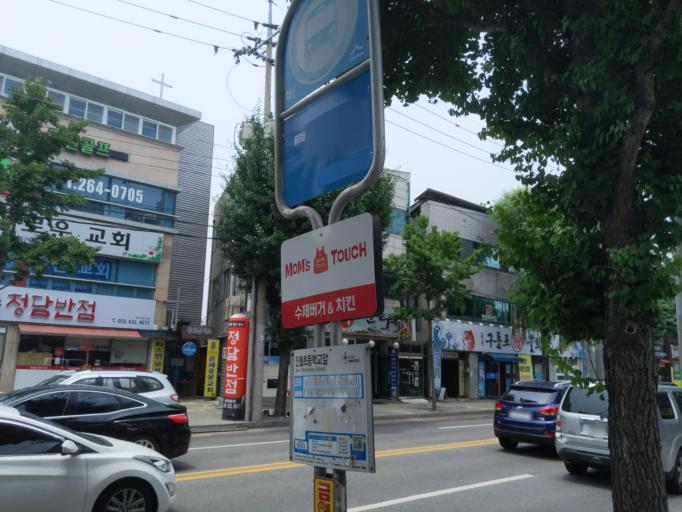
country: KR
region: Daegu
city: Hwawon
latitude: 35.8099
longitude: 128.5265
